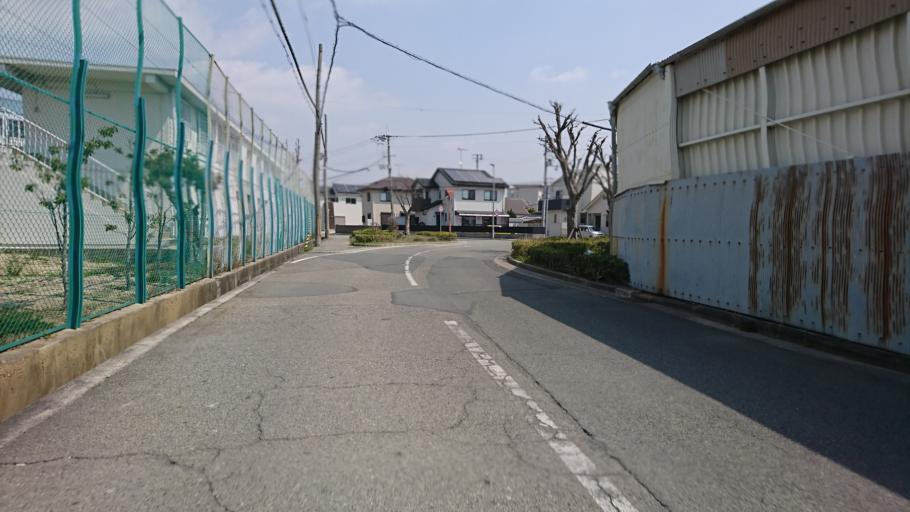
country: JP
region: Hyogo
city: Kakogawacho-honmachi
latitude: 34.7708
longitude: 134.7778
